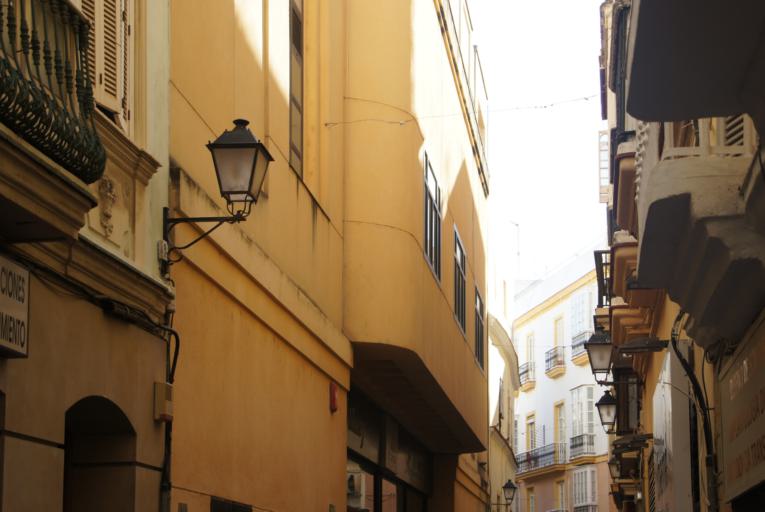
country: ES
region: Andalusia
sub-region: Provincia de Cadiz
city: Cadiz
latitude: 36.5320
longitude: -6.2971
